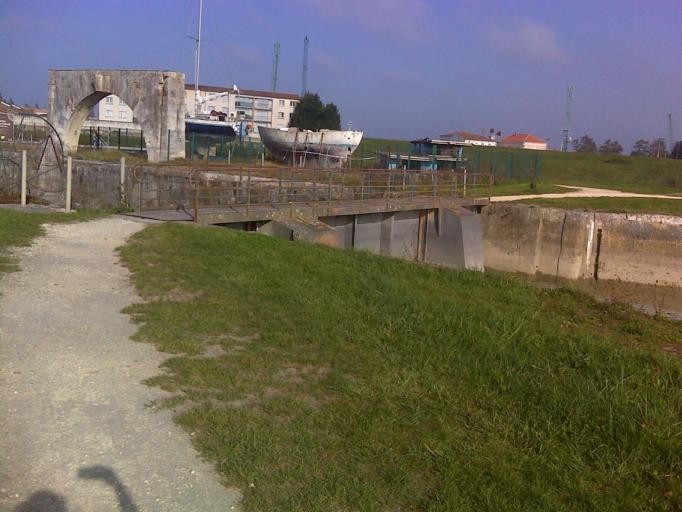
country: FR
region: Poitou-Charentes
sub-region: Departement de la Charente-Maritime
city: Rochefort
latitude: 45.9444
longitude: -0.9539
